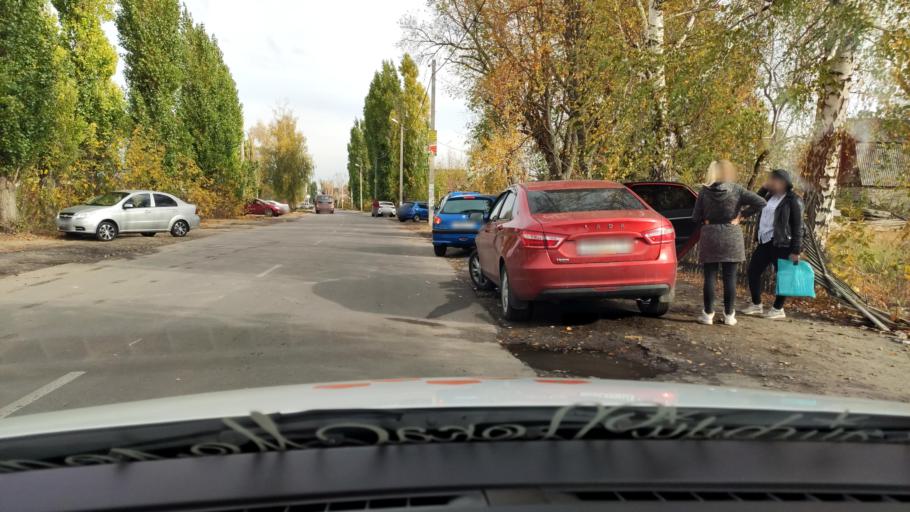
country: RU
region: Voronezj
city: Ramon'
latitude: 51.9157
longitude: 39.3416
